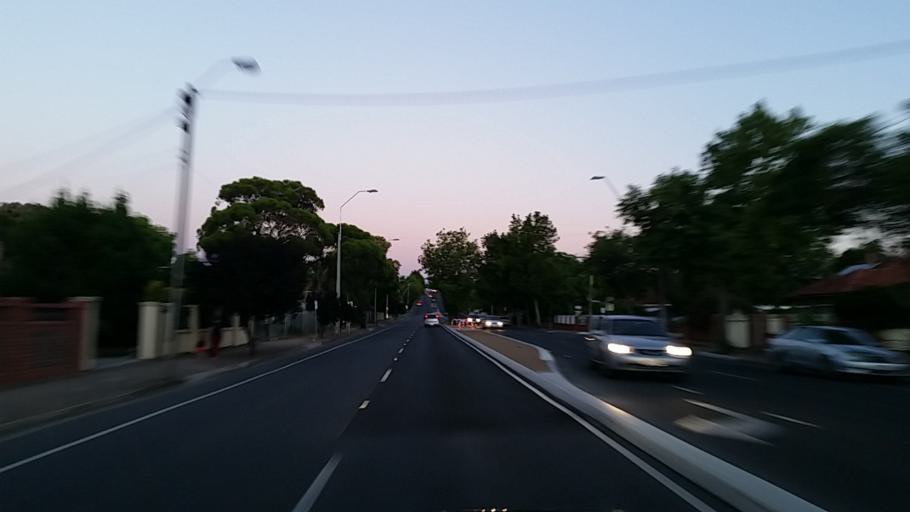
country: AU
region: South Australia
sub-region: Prospect
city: Prospect
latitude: -34.8743
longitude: 138.5881
